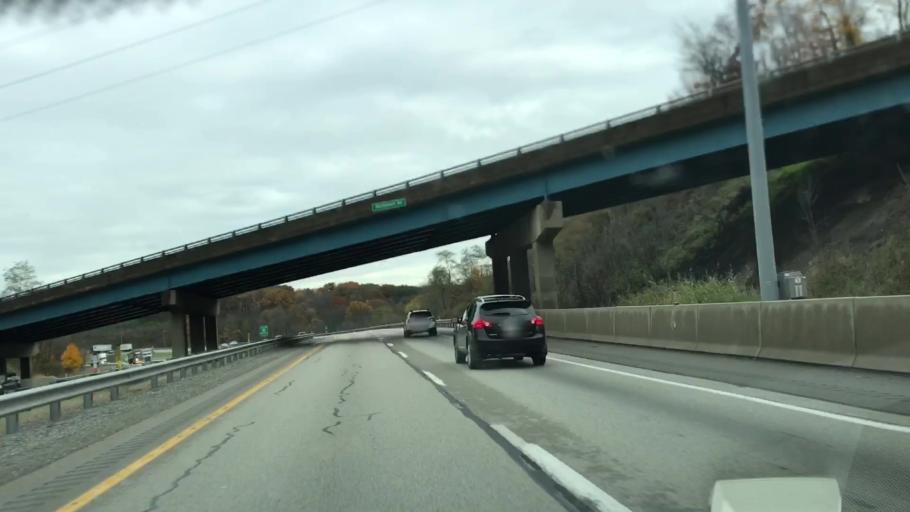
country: US
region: Pennsylvania
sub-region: Allegheny County
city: Franklin Park
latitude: 40.5830
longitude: -80.1055
